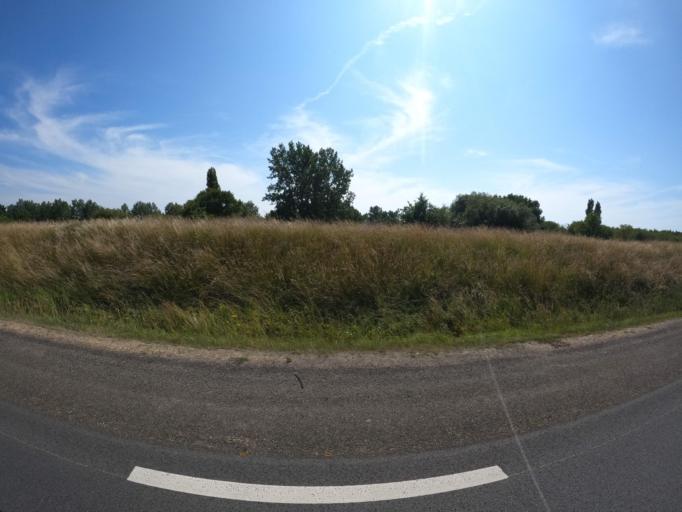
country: FR
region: Pays de la Loire
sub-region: Departement de la Loire-Atlantique
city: Bourgneuf-en-Retz
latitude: 47.0530
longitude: -1.9666
